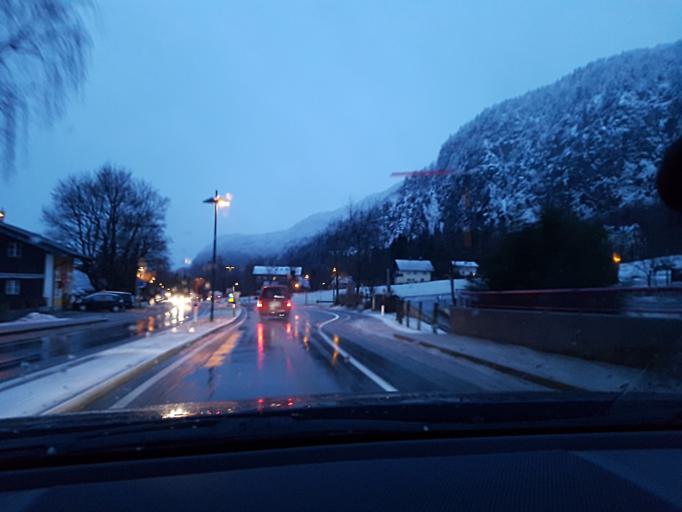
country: AT
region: Salzburg
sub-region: Politischer Bezirk Salzburg-Umgebung
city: Sankt Gilgen
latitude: 47.7640
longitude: 13.3648
